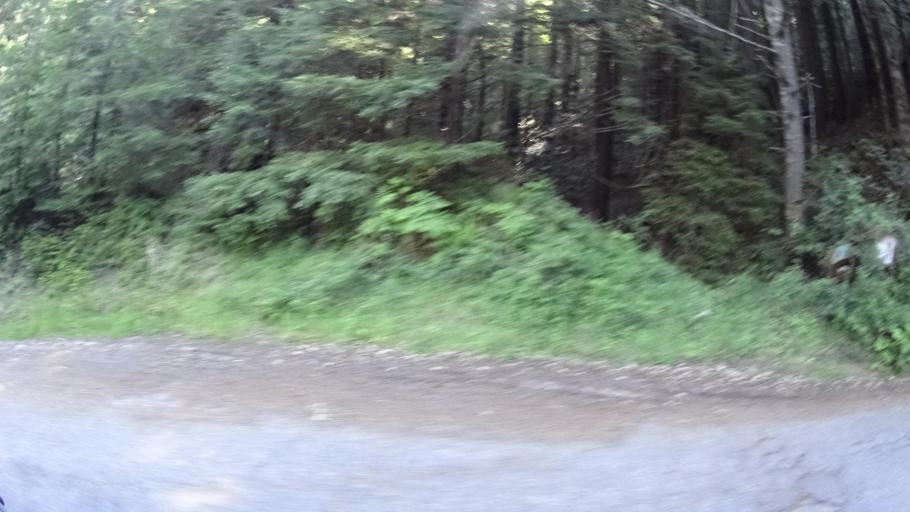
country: US
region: California
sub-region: Humboldt County
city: Rio Dell
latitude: 40.4534
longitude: -123.9800
